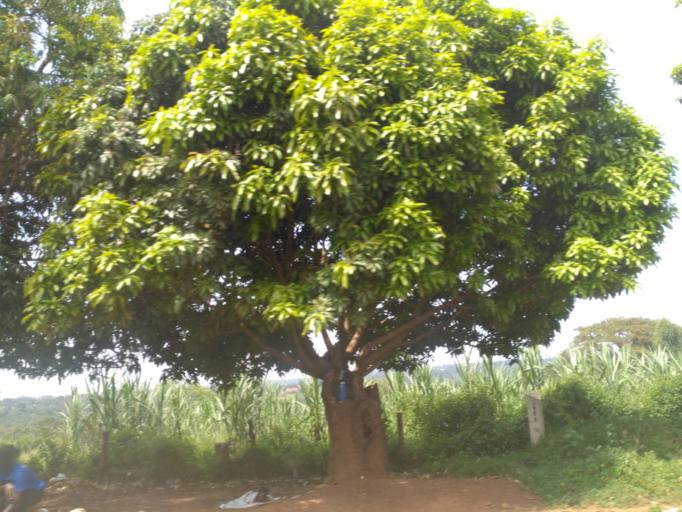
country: UG
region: Central Region
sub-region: Wakiso District
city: Bweyogerere
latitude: 0.4704
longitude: 32.6058
